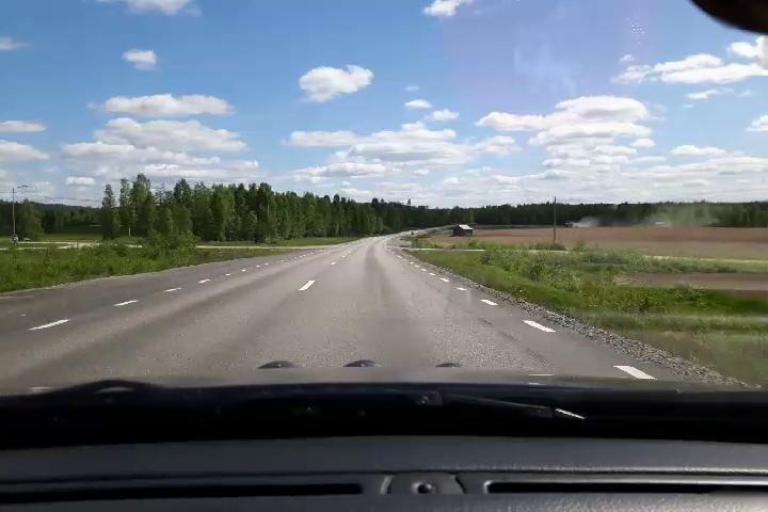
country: SE
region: Gaevleborg
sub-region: Ljusdals Kommun
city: Farila
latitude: 61.8642
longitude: 15.7369
